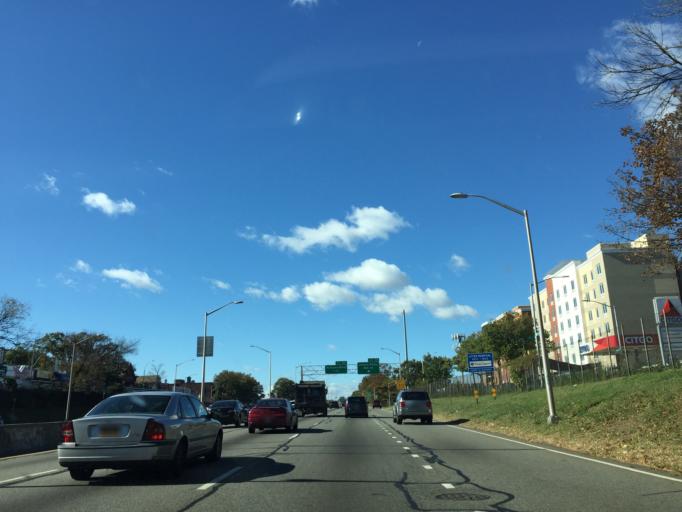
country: US
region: New York
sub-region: Queens County
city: Jamaica
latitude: 40.7404
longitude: -73.7889
